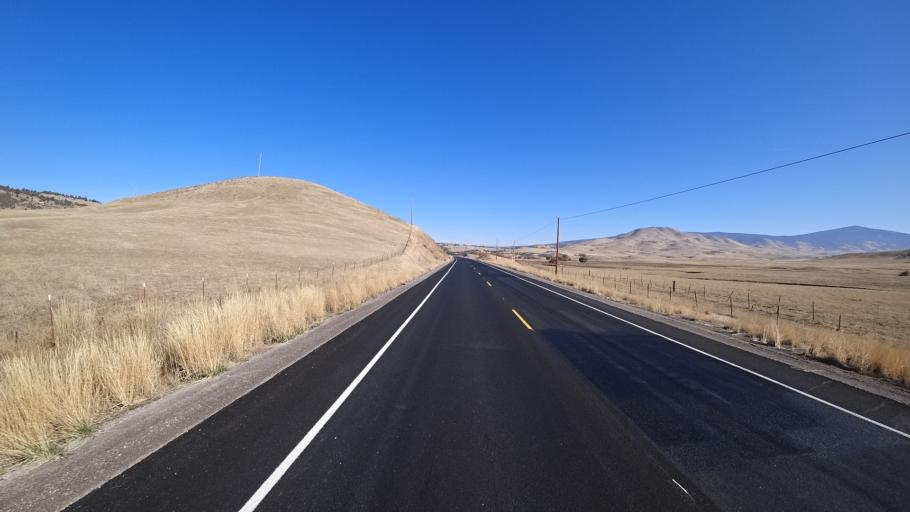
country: US
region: California
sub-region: Siskiyou County
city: Montague
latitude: 41.8364
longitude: -122.4838
